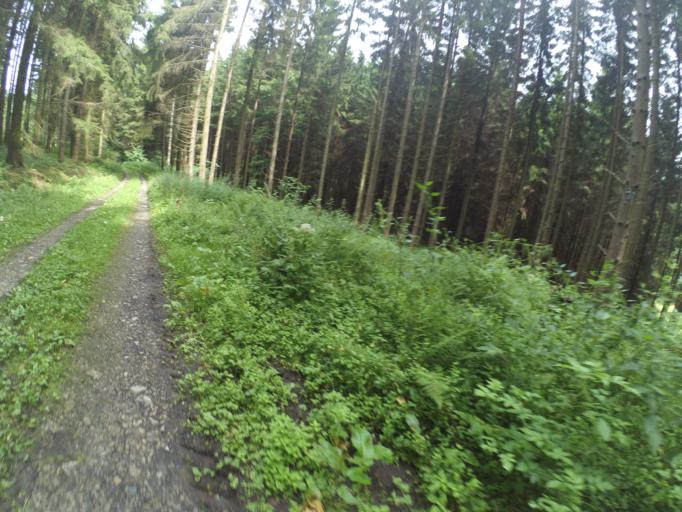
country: DE
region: Hesse
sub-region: Regierungsbezirk Kassel
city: Kirchheim
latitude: 50.8651
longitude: 9.5377
